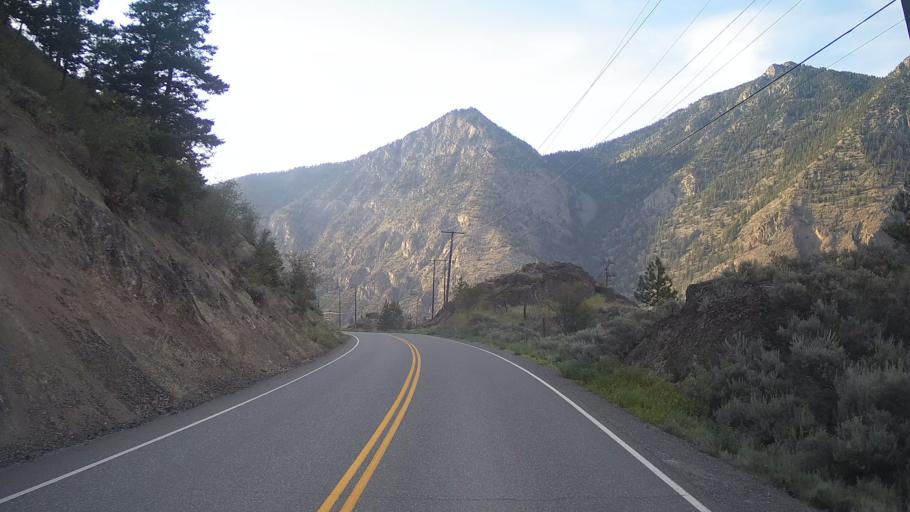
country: CA
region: British Columbia
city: Lillooet
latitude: 50.7523
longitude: -121.8937
